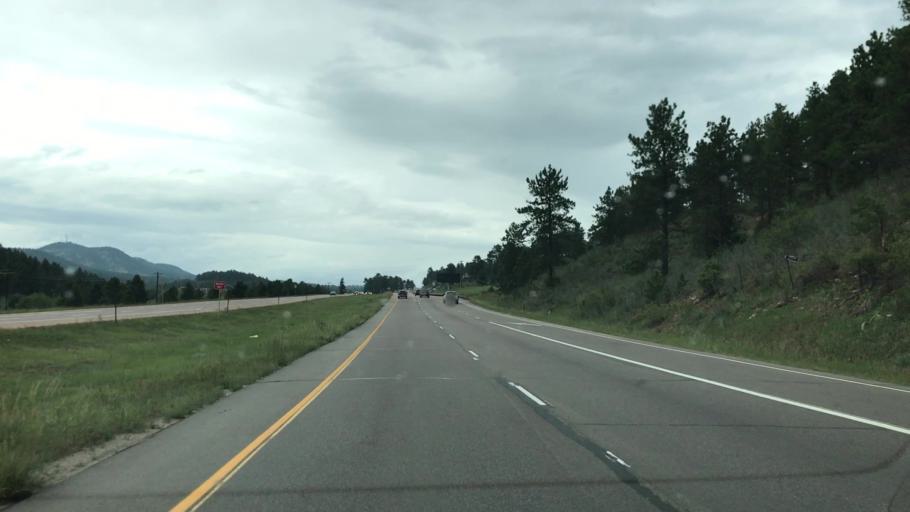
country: US
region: Colorado
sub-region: El Paso County
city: Cascade-Chipita Park
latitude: 38.9635
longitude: -105.0306
